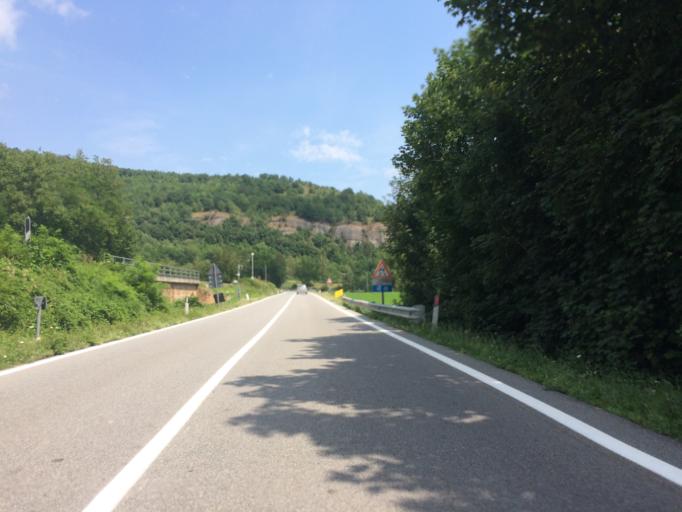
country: IT
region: Piedmont
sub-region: Provincia di Cuneo
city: Bagnasco
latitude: 44.2917
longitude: 8.0351
